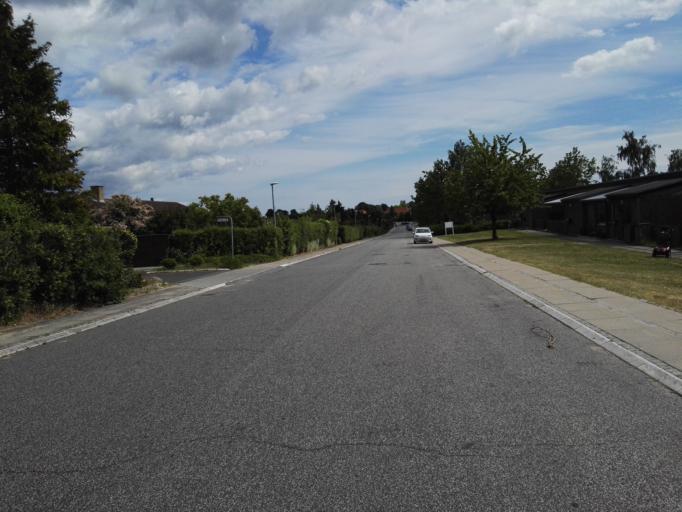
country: DK
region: Capital Region
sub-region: Egedal Kommune
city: Stenlose
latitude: 55.7726
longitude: 12.1907
